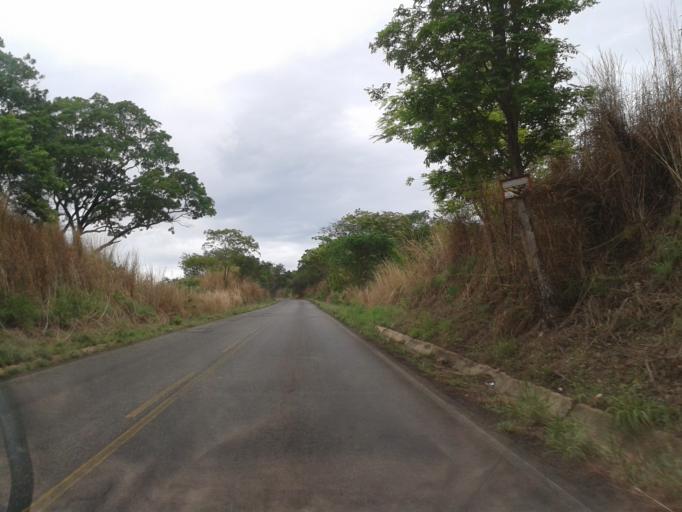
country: BR
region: Goias
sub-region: Buriti Alegre
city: Buriti Alegre
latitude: -18.0580
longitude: -48.7346
